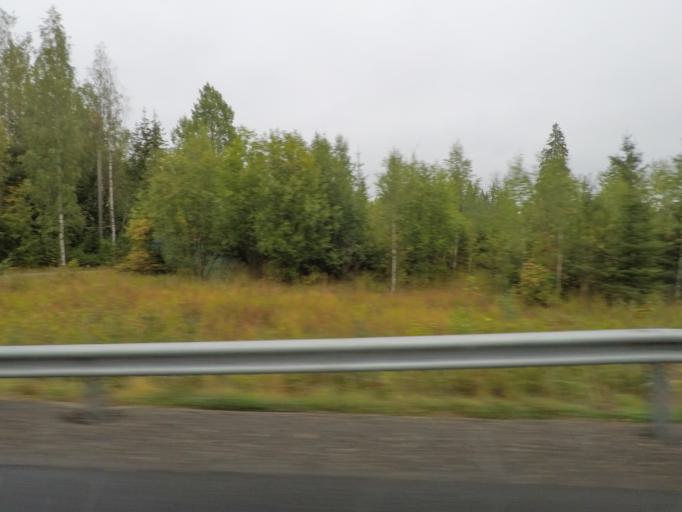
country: FI
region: Northern Savo
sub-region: Varkaus
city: Leppaevirta
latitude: 62.5113
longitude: 27.7069
